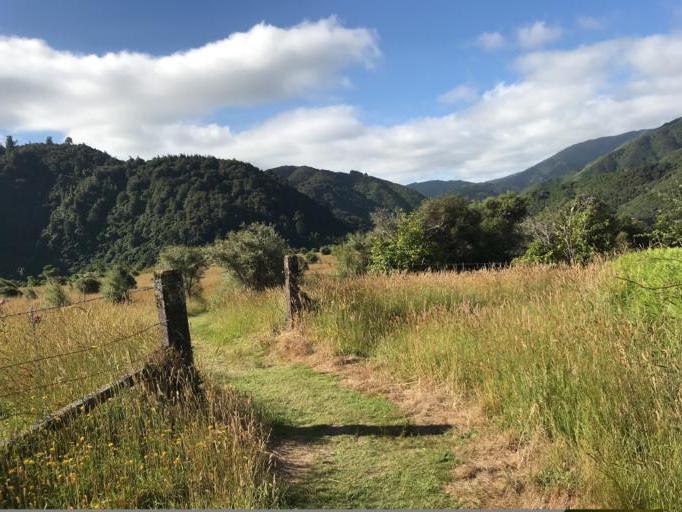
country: NZ
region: Wellington
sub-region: Kapiti Coast District
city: Otaki
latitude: -40.8746
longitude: 175.2350
